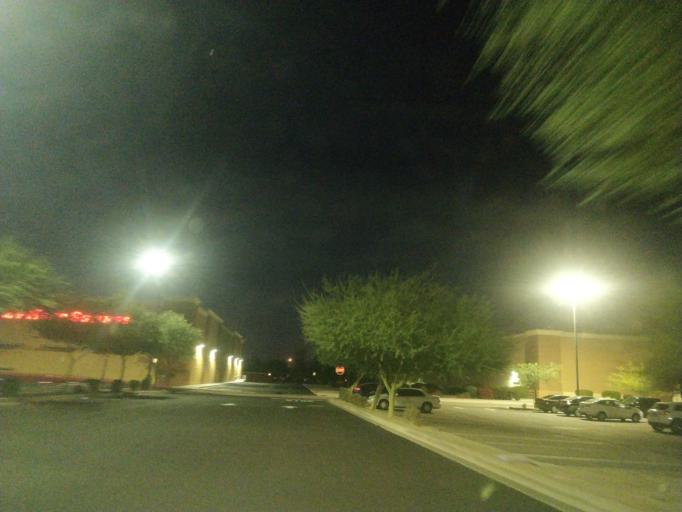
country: US
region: Arizona
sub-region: Maricopa County
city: Chandler
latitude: 33.2848
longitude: -111.8445
